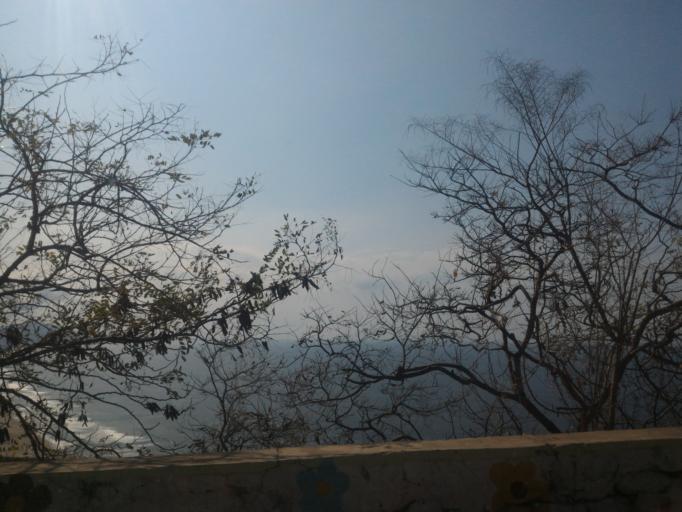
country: MX
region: Michoacan
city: Coahuayana Viejo
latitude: 18.5632
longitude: -103.6472
